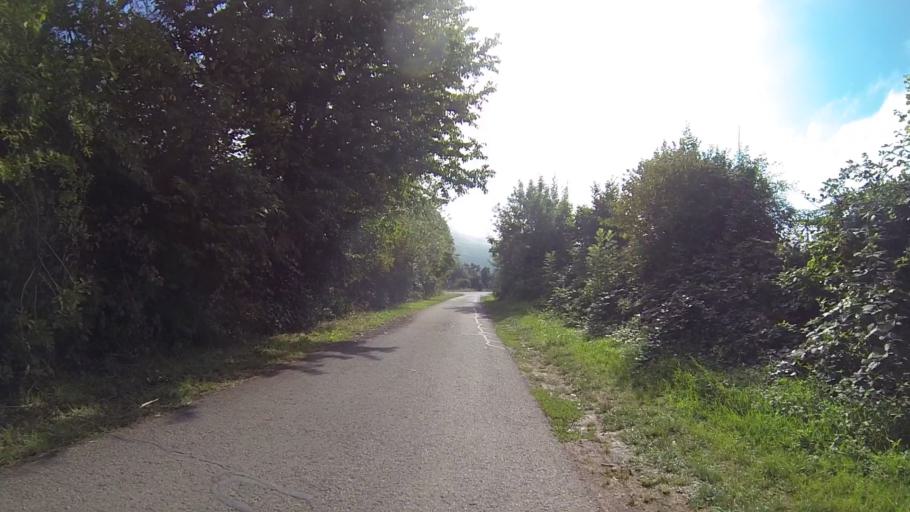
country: DE
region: Rheinland-Pfalz
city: Schweich
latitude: 49.8133
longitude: 6.7592
